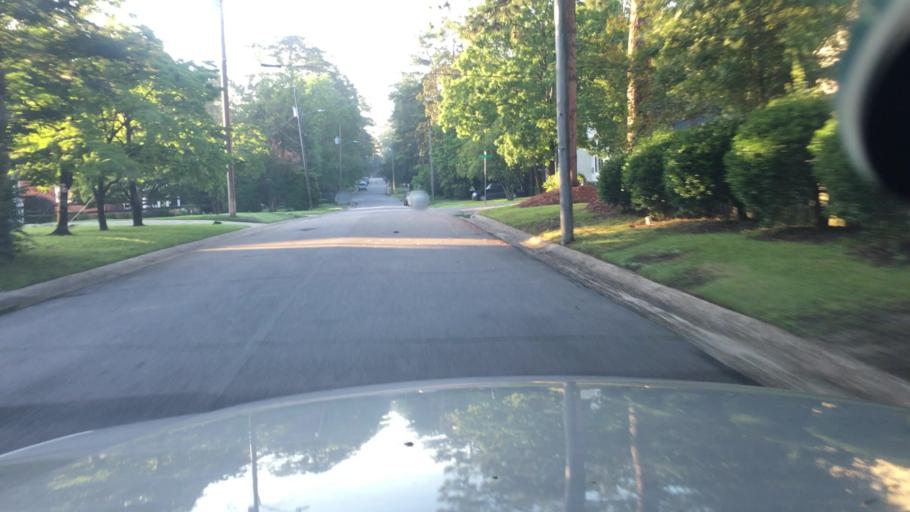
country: US
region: North Carolina
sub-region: Cumberland County
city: Fayetteville
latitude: 35.0639
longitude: -78.9180
